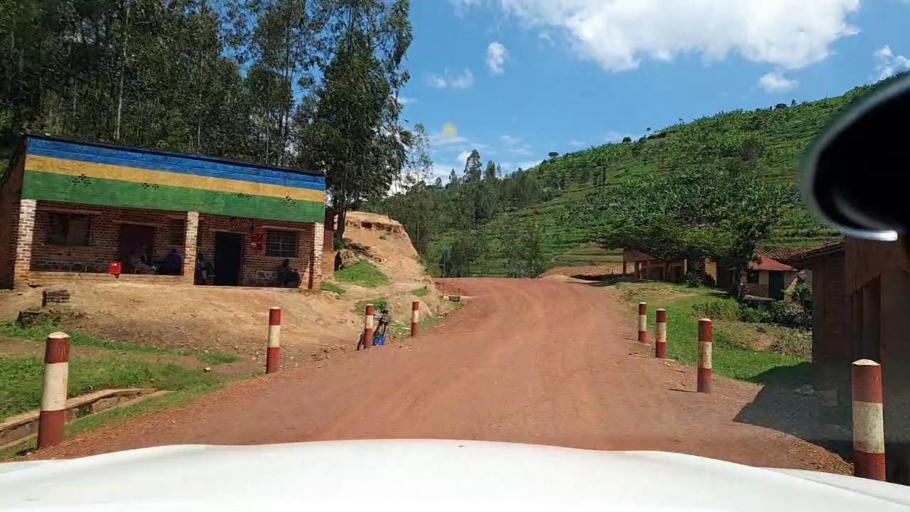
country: RW
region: Kigali
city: Kigali
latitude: -1.7588
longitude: 29.8693
